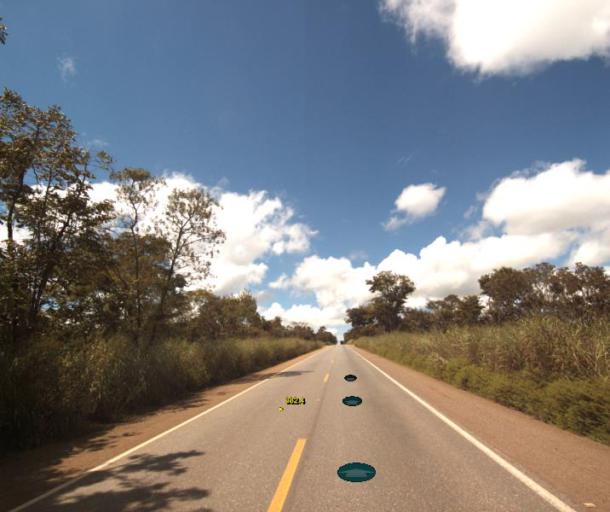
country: BR
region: Goias
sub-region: Jaragua
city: Jaragua
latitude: -15.9152
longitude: -49.2207
